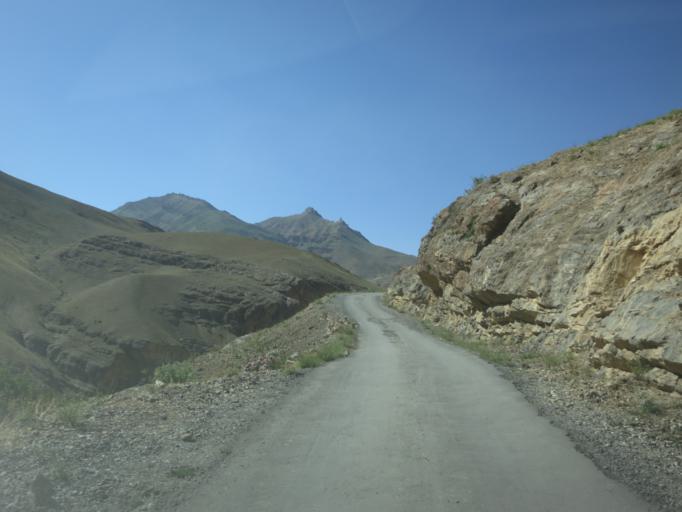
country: IN
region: Himachal Pradesh
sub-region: Kulu
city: Manali
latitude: 32.3212
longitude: 78.0015
